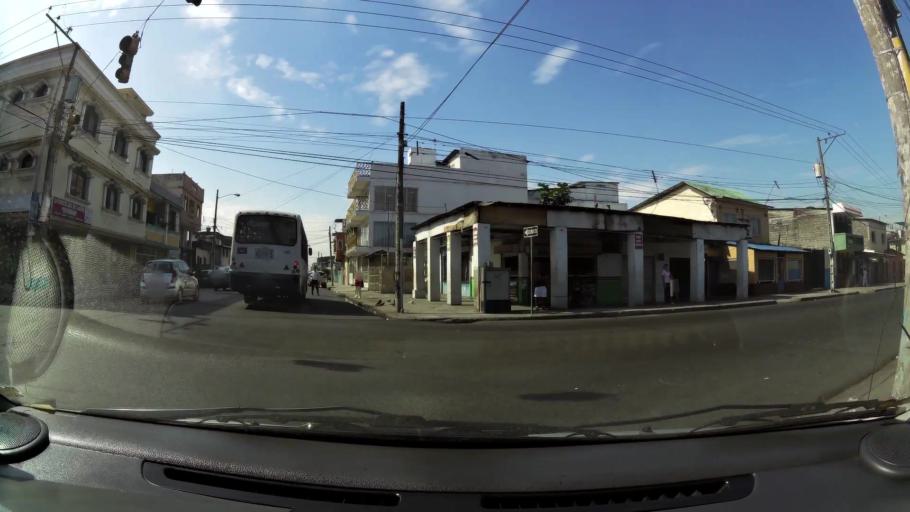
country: EC
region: Guayas
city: Guayaquil
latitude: -2.2181
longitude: -79.9004
